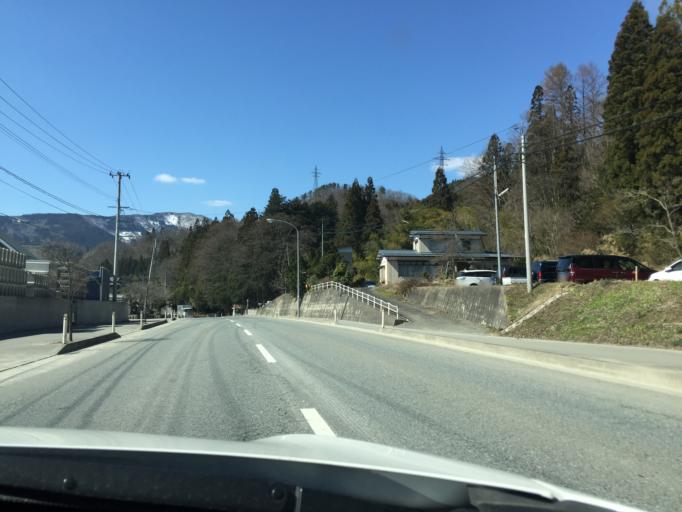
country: JP
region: Yamagata
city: Nagai
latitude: 38.2244
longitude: 140.0980
